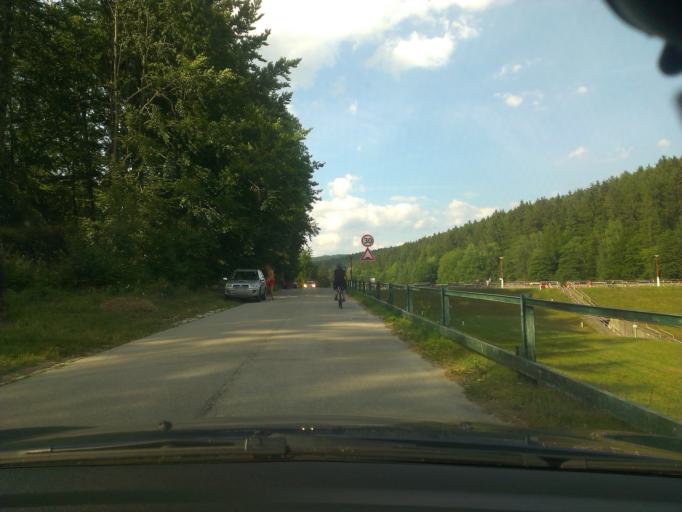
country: SK
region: Trenciansky
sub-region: Okres Myjava
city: Myjava
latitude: 48.8088
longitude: 17.5940
